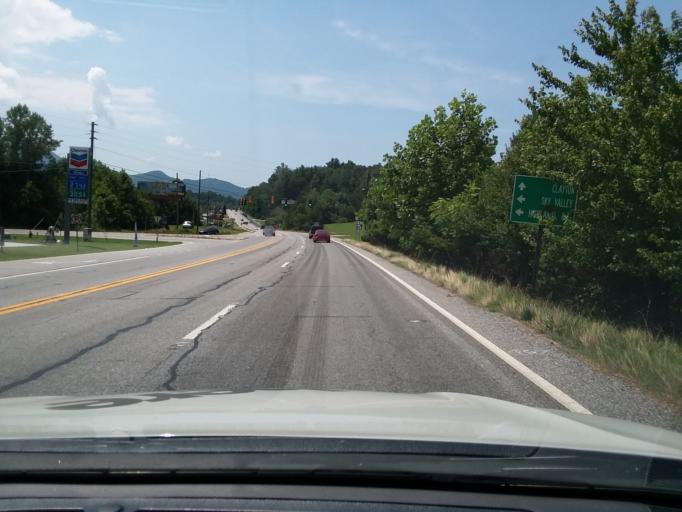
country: US
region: Georgia
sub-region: Rabun County
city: Mountain City
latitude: 34.9850
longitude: -83.3847
